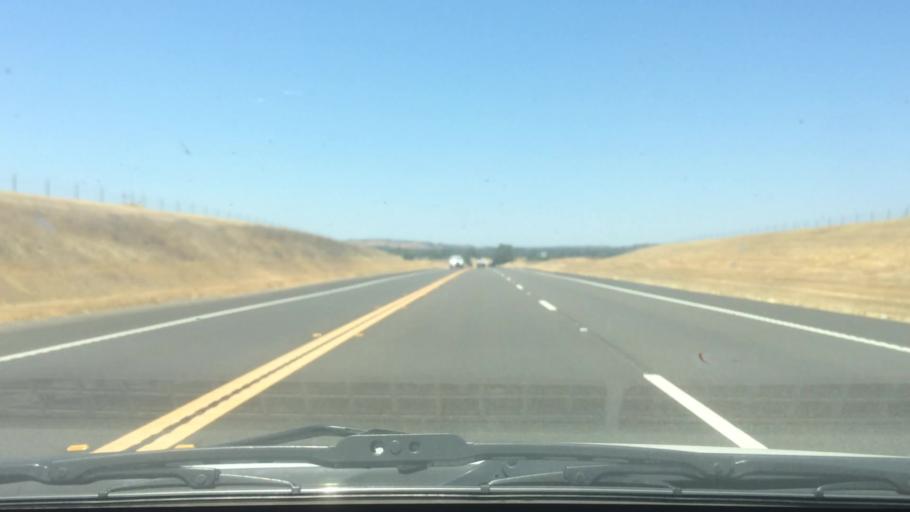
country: US
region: California
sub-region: Santa Barbara County
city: Santa Ynez
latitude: 34.6148
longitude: -120.0602
